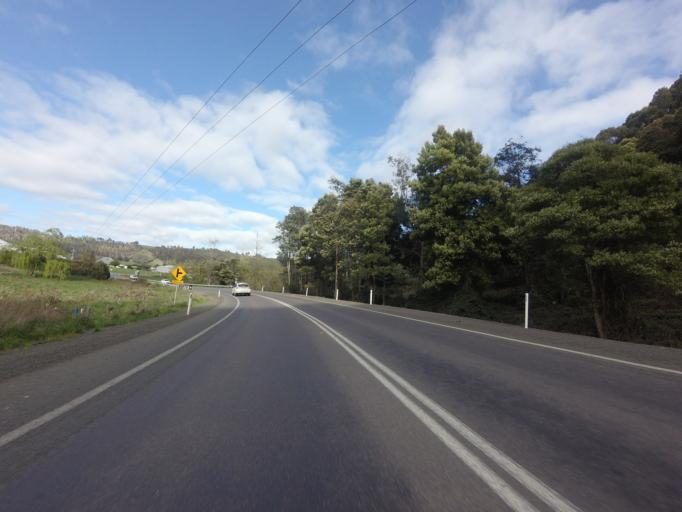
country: AU
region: Tasmania
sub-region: Huon Valley
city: Franklin
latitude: -43.1313
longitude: 146.9778
